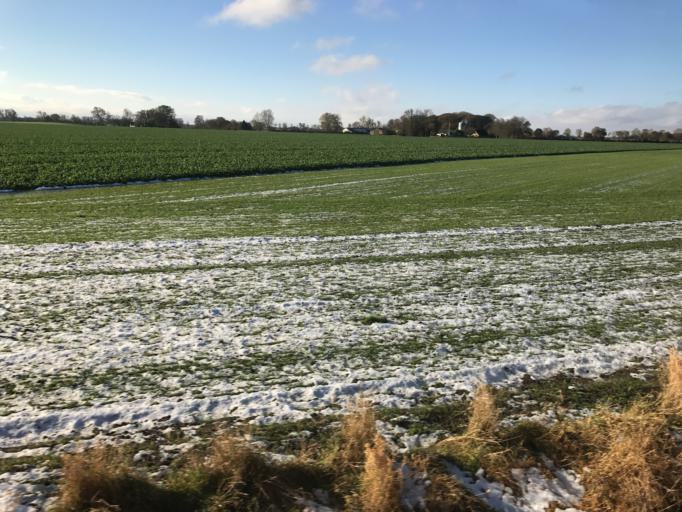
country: DK
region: Zealand
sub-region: Stevns Kommune
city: Store Heddinge
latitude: 55.3425
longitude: 12.3322
